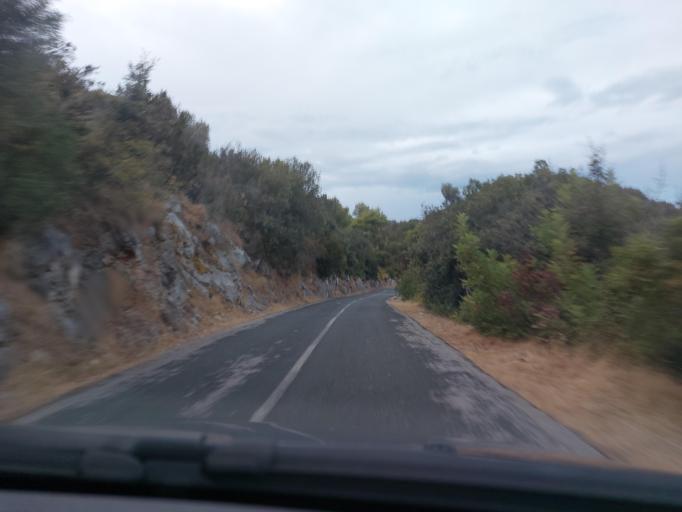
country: HR
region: Dubrovacko-Neretvanska
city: Smokvica
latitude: 42.7701
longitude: 16.8787
